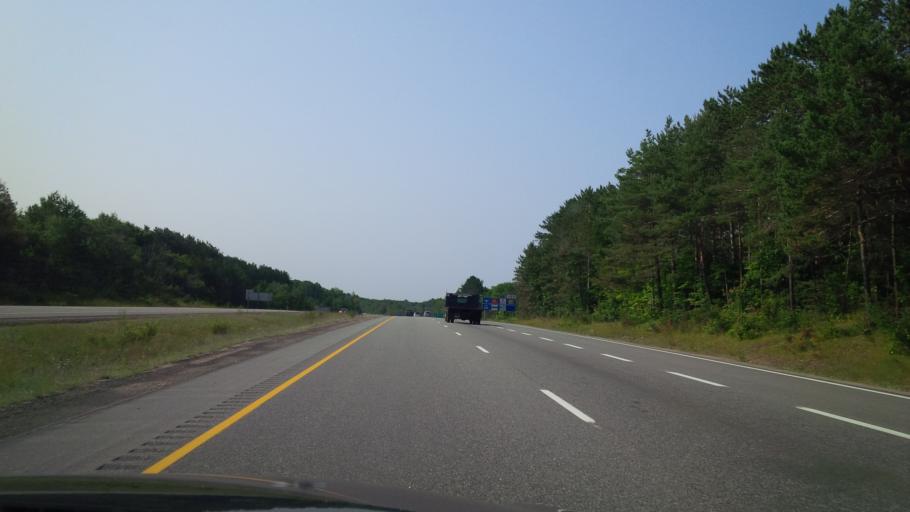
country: CA
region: Ontario
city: Bracebridge
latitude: 45.0708
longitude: -79.2971
